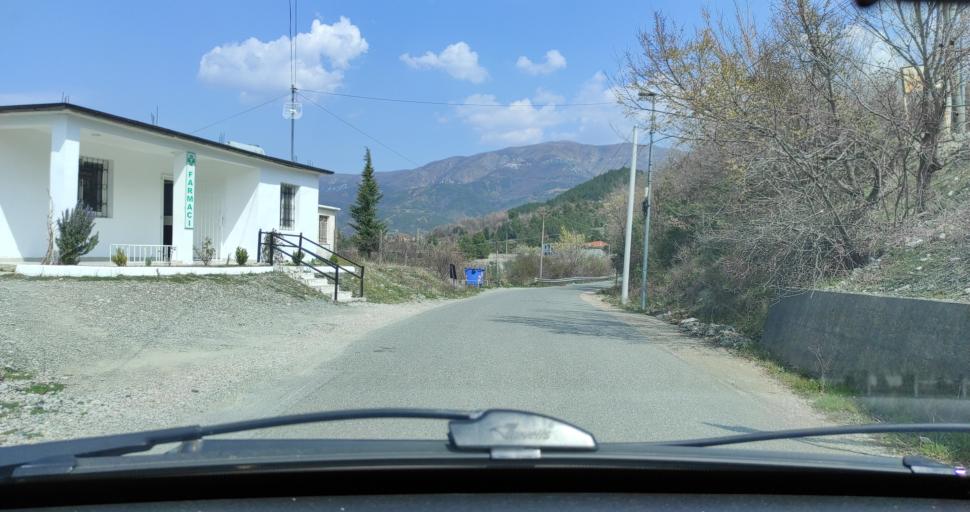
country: AL
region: Lezhe
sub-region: Rrethi i Lezhes
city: Kallmeti i Madh
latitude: 41.8508
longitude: 19.6919
